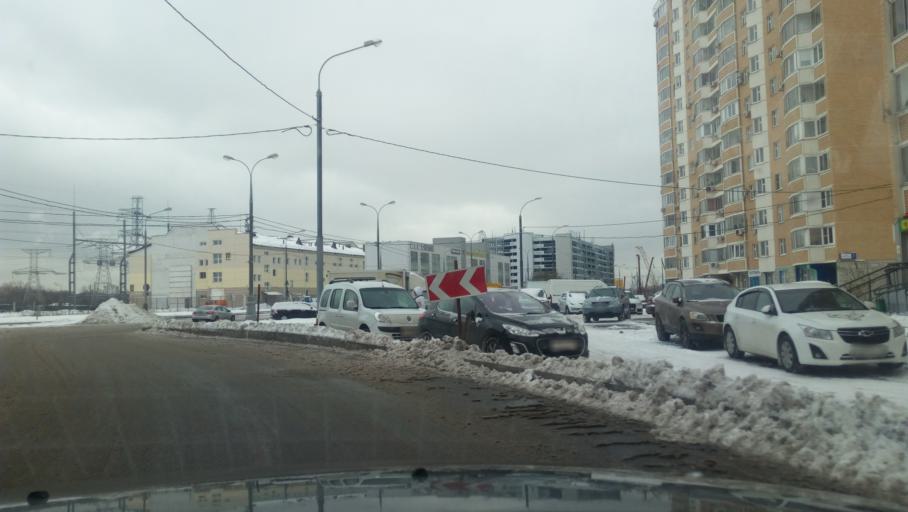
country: RU
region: Moscow
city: Nekrasovka
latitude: 55.7087
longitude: 37.8884
